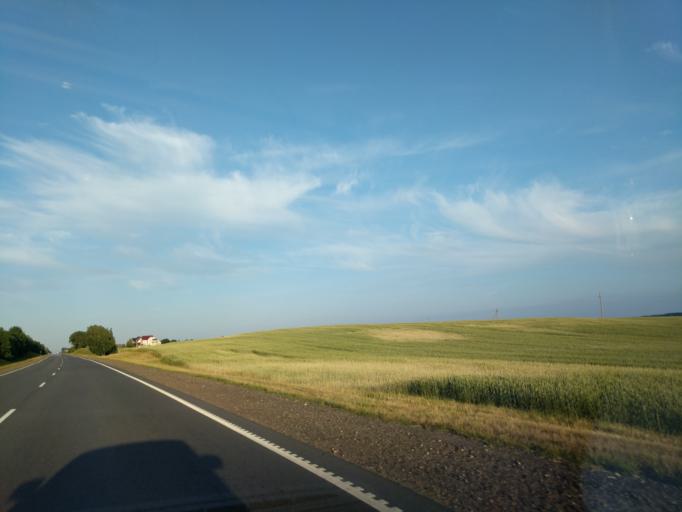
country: BY
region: Minsk
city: Syomkava
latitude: 54.0995
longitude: 27.4871
